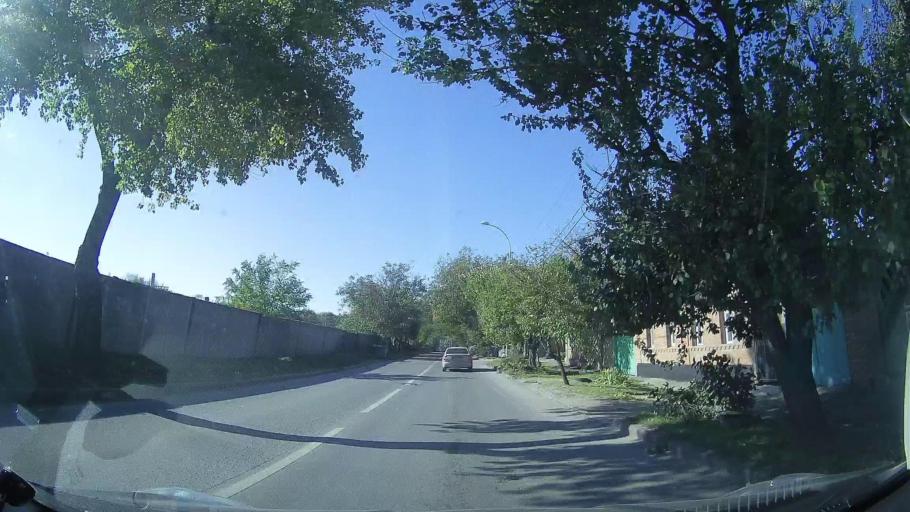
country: RU
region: Rostov
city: Rostov-na-Donu
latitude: 47.2256
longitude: 39.6776
